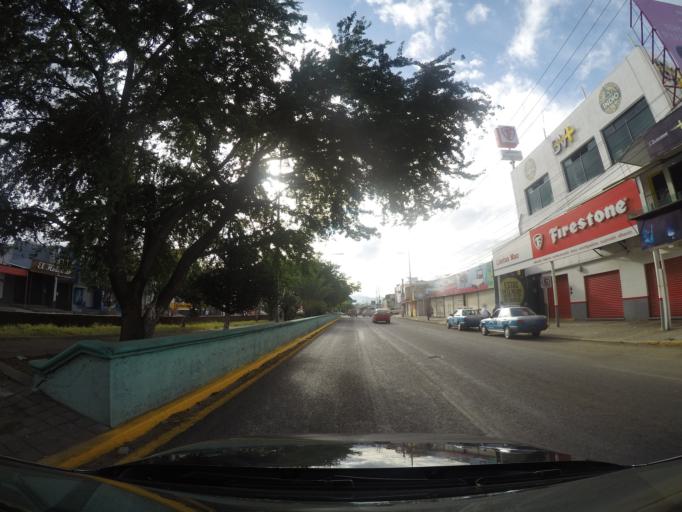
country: MX
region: Oaxaca
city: Oaxaca de Juarez
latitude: 17.0695
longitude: -96.7033
